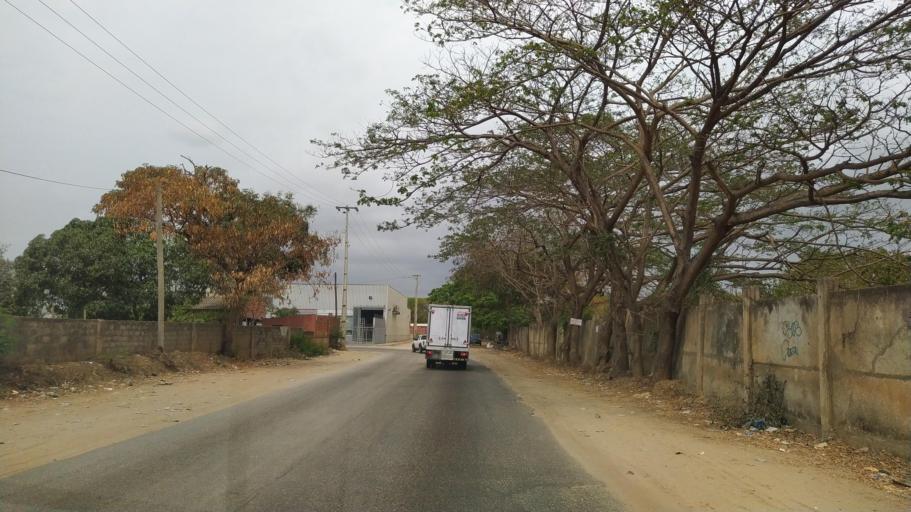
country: AO
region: Luanda
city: Luanda
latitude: -8.8576
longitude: 13.2881
